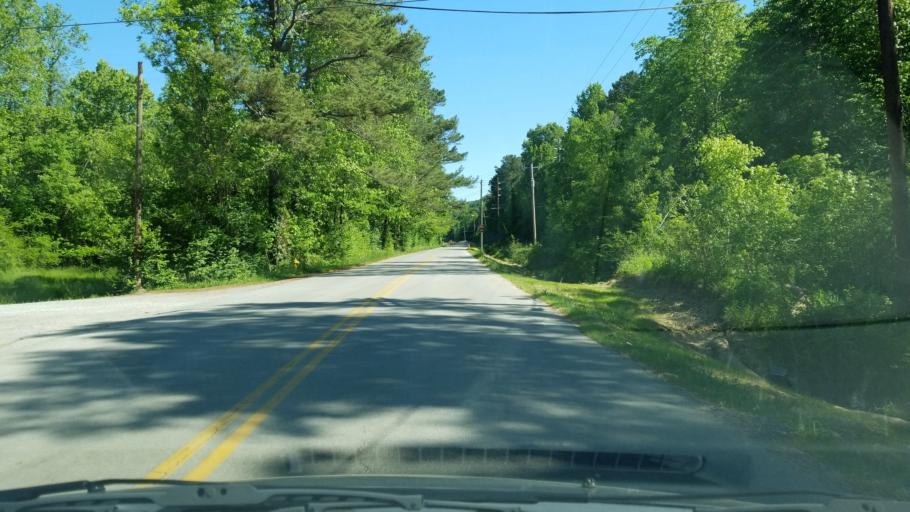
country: US
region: Tennessee
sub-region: Hamilton County
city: Chattanooga
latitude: 35.0398
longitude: -85.3343
